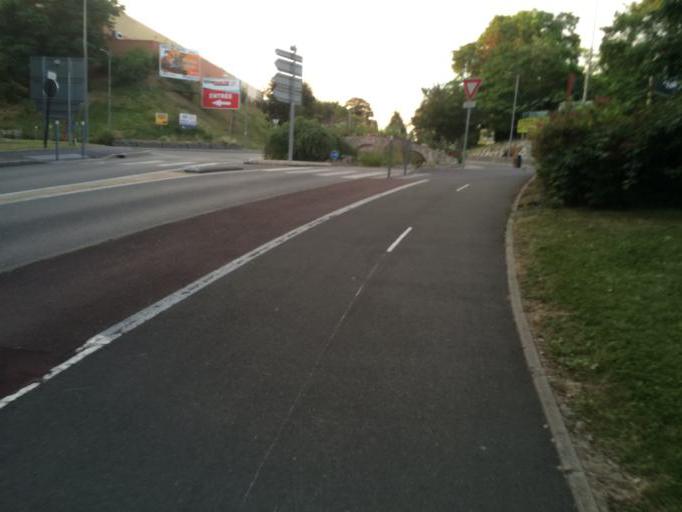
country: FR
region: Ile-de-France
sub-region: Departement de l'Essonne
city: Longjumeau
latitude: 48.7037
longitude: 2.2968
